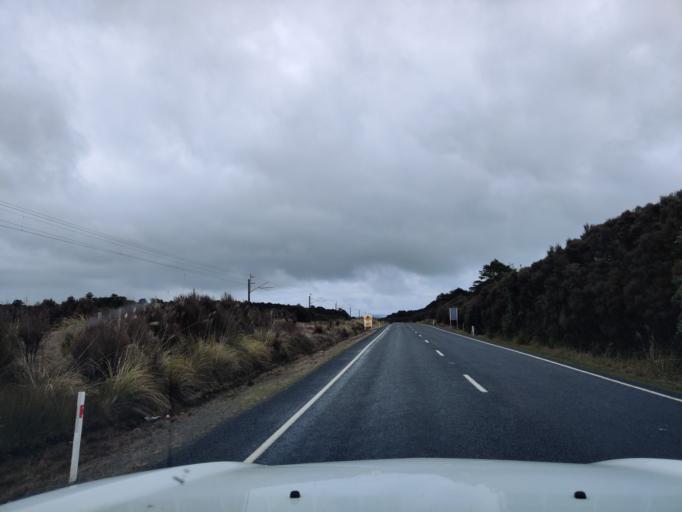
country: NZ
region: Manawatu-Wanganui
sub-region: Ruapehu District
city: Waiouru
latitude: -39.3252
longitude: 175.3842
